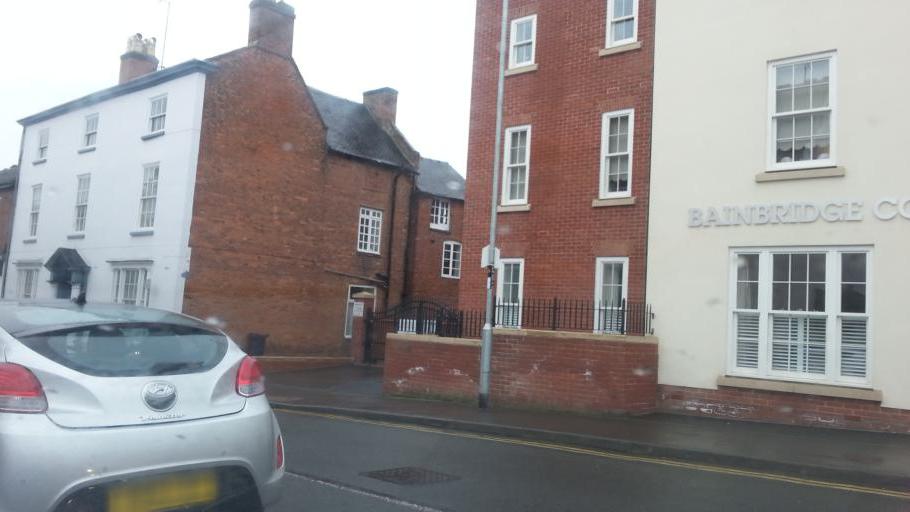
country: GB
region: England
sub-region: Leicestershire
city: Ashby de la Zouch
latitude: 52.7465
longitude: -1.4747
